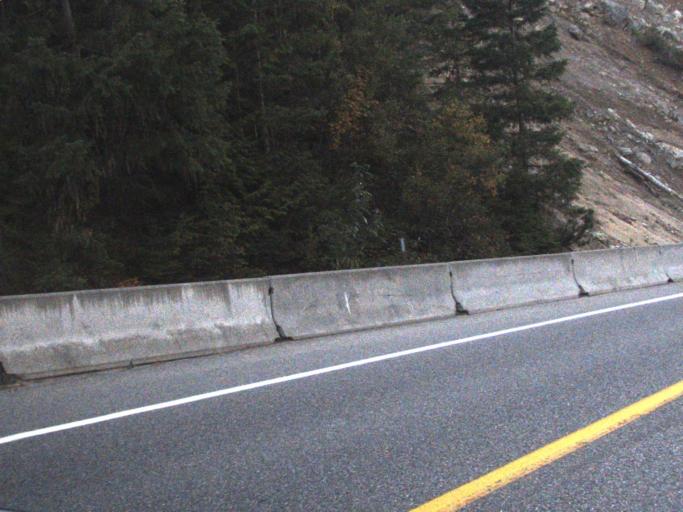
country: US
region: Washington
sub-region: Snohomish County
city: Darrington
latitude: 48.6625
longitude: -120.8682
